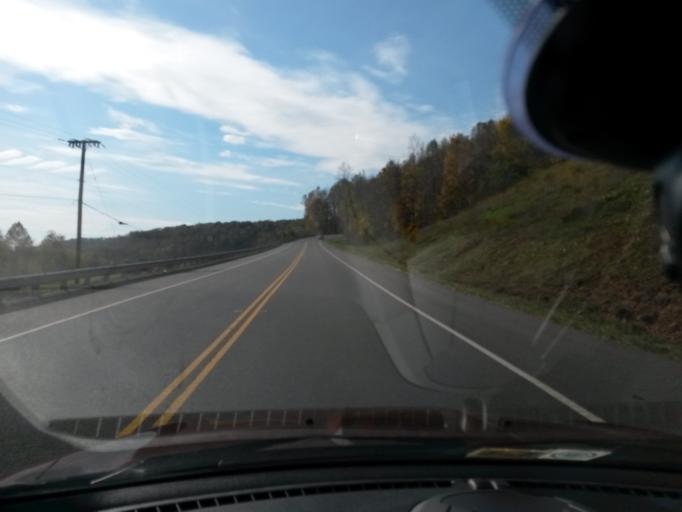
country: US
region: Virginia
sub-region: Franklin County
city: North Shore
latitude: 37.1242
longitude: -79.7828
